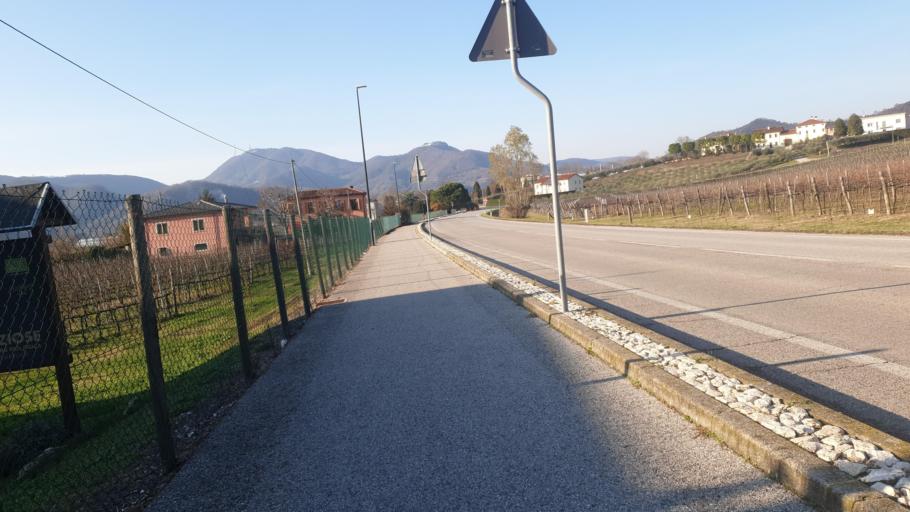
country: IT
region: Veneto
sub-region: Provincia di Padova
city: Battaglia Terme
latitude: 45.2978
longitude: 11.7601
